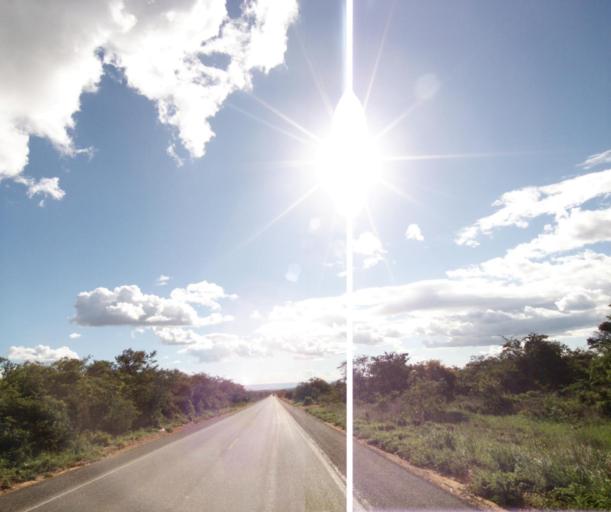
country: BR
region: Bahia
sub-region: Caetite
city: Caetite
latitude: -14.1272
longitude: -42.6222
